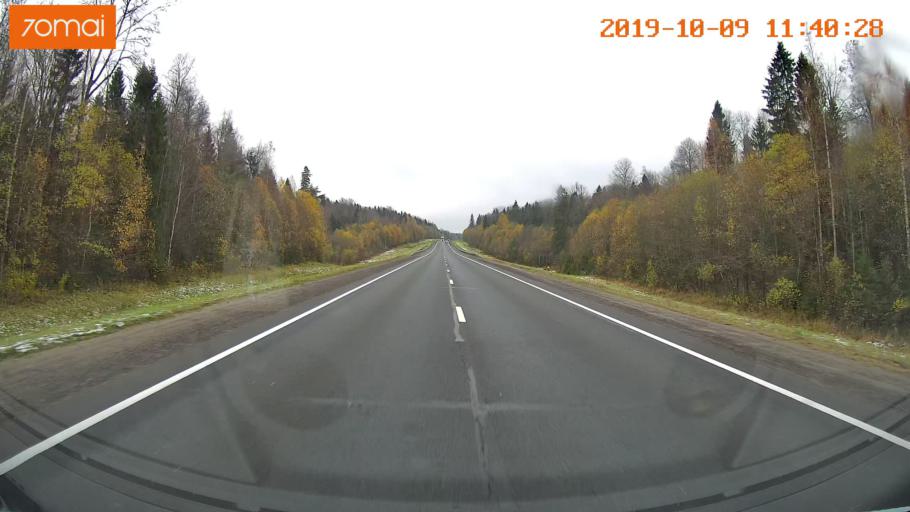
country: RU
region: Vologda
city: Gryazovets
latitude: 58.9419
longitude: 40.1742
